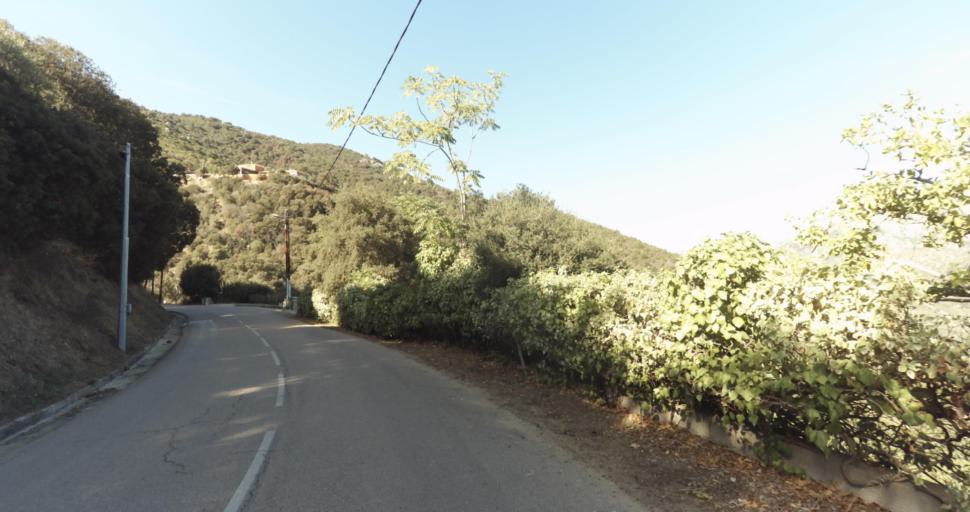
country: FR
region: Corsica
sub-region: Departement de la Corse-du-Sud
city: Ajaccio
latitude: 41.9258
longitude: 8.7103
